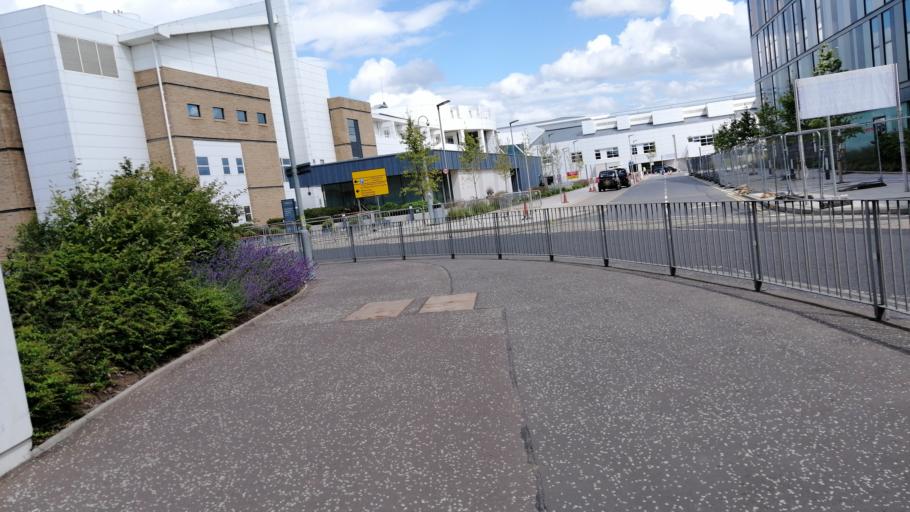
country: GB
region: Scotland
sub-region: West Lothian
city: Seafield
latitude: 55.9217
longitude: -3.1387
